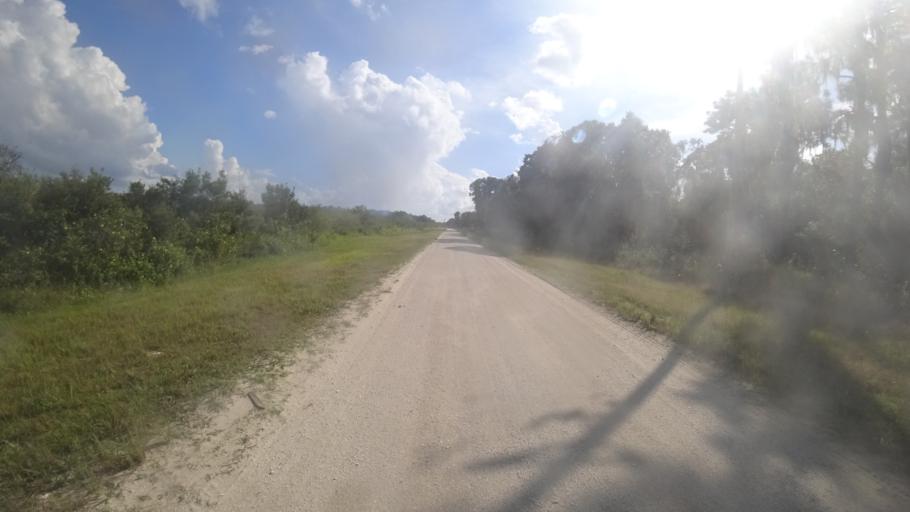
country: US
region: Florida
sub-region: Hillsborough County
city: Balm
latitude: 27.6172
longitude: -82.1198
